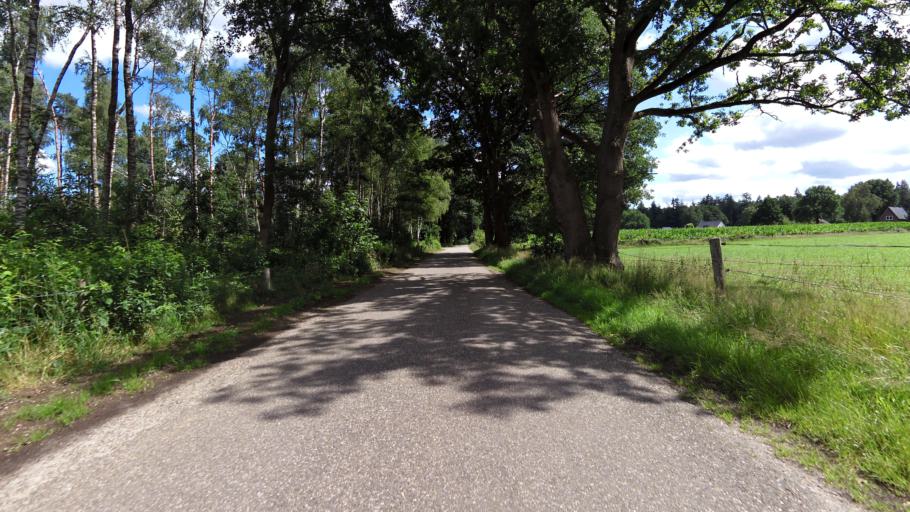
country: NL
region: Gelderland
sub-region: Gemeente Epe
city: Vaassen
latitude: 52.2498
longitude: 5.9415
